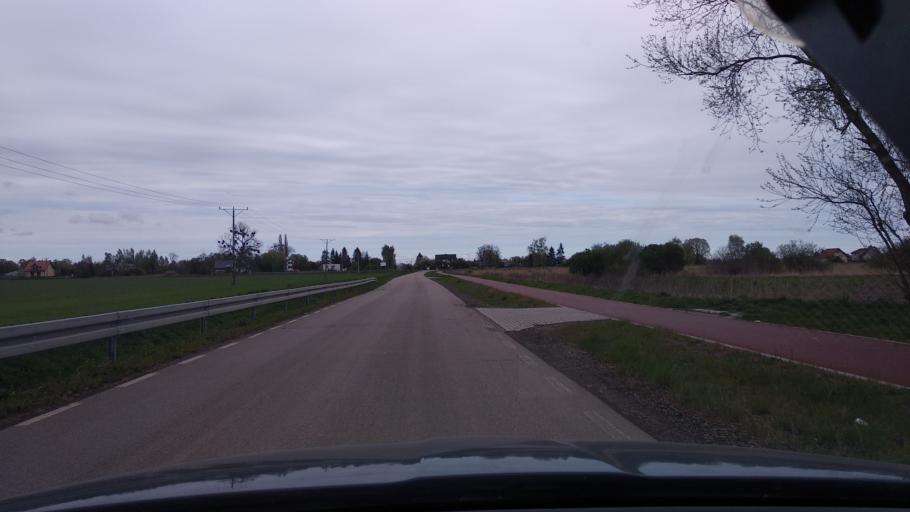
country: PL
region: Pomeranian Voivodeship
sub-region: Powiat gdanski
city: Pruszcz Gdanski
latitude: 54.2739
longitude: 18.6608
